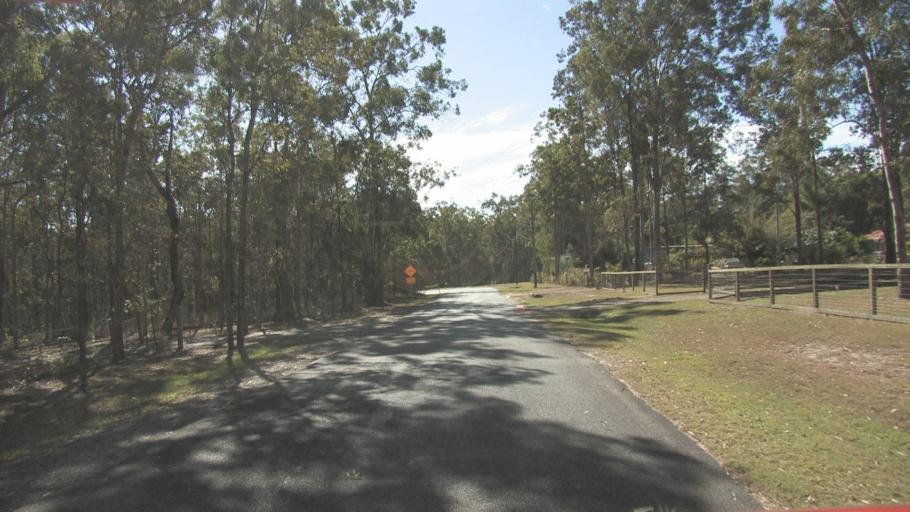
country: AU
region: Queensland
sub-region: Ipswich
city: Springfield Lakes
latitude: -27.7128
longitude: 152.9602
